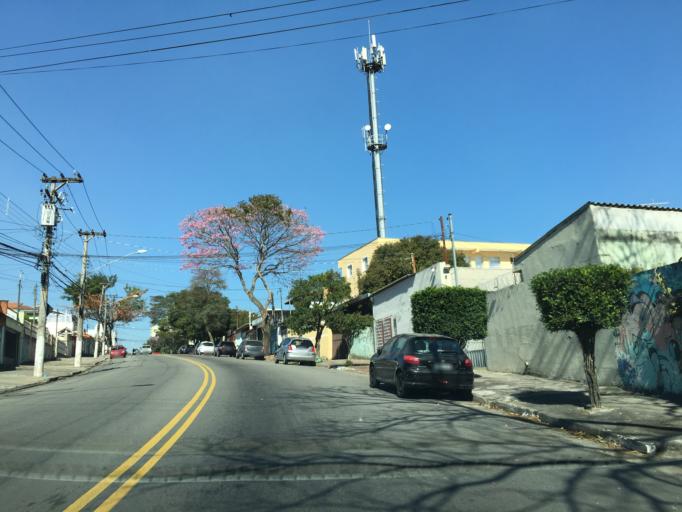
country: BR
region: Sao Paulo
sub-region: Osasco
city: Osasco
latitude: -23.5661
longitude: -46.7479
